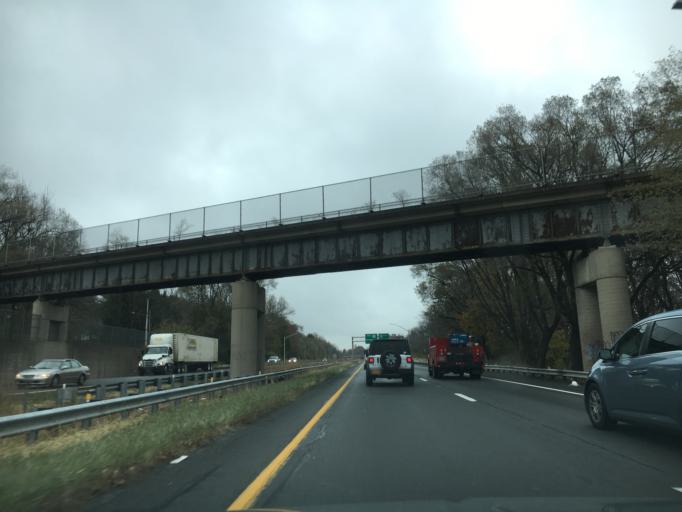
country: US
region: Pennsylvania
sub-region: Lehigh County
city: Fountain Hill
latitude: 40.6325
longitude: -75.4086
